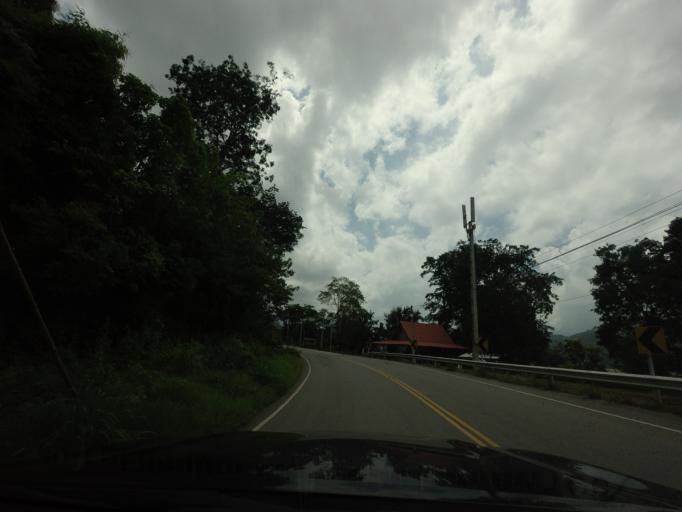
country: TH
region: Loei
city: Pak Chom
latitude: 18.0560
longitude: 101.7763
